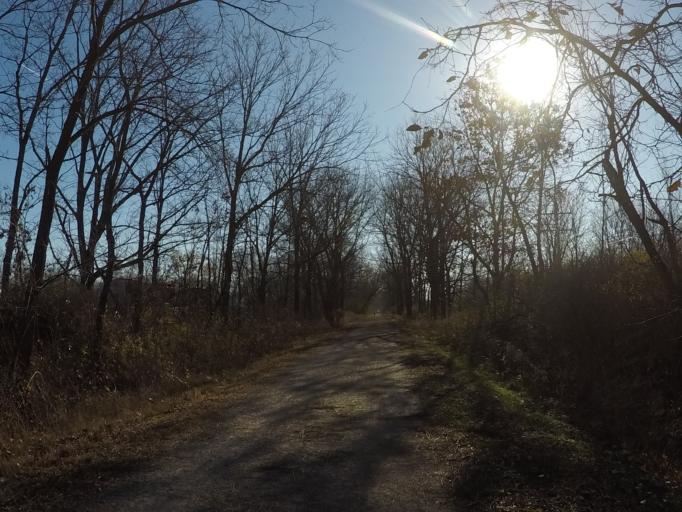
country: US
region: Wisconsin
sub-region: Dane County
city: Deerfield
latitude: 43.0520
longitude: -89.0661
